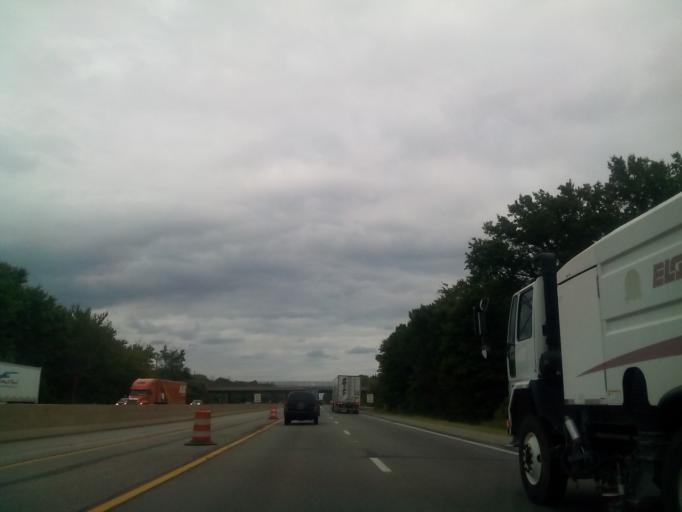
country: US
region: Ohio
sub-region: Lorain County
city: Elyria
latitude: 41.3899
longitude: -82.1526
